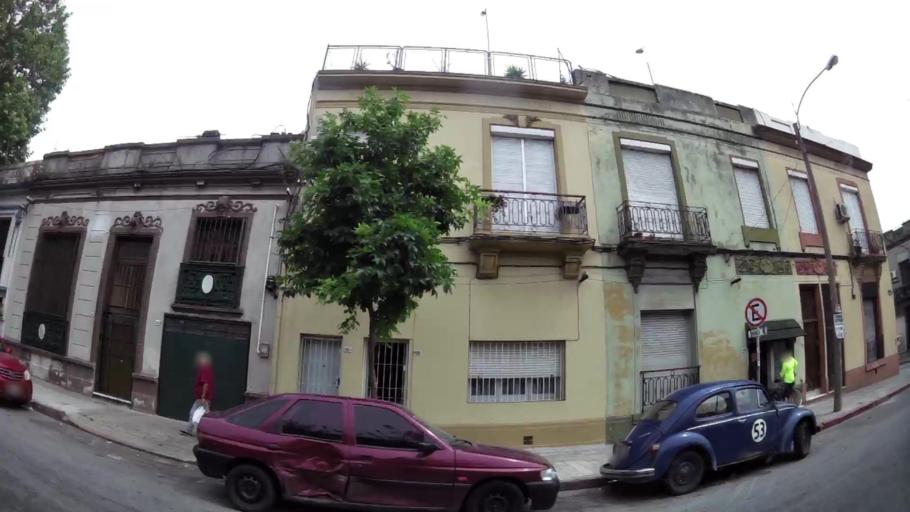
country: UY
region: Montevideo
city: Montevideo
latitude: -34.8980
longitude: -56.1774
